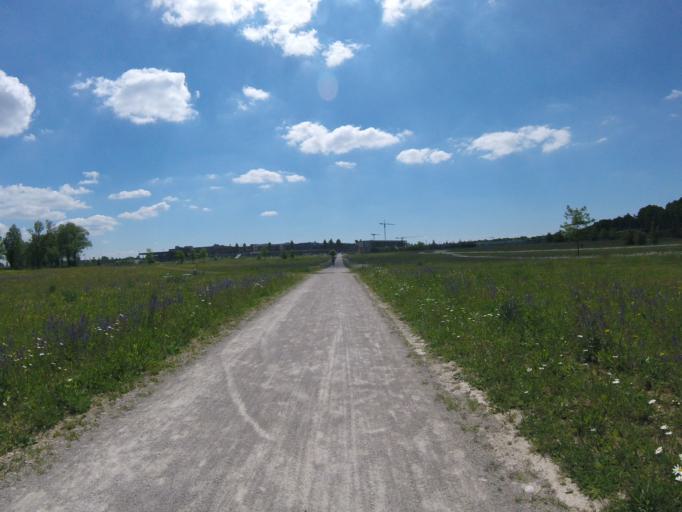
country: DE
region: Bavaria
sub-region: Upper Bavaria
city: Unterhaching
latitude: 48.0824
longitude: 11.6097
